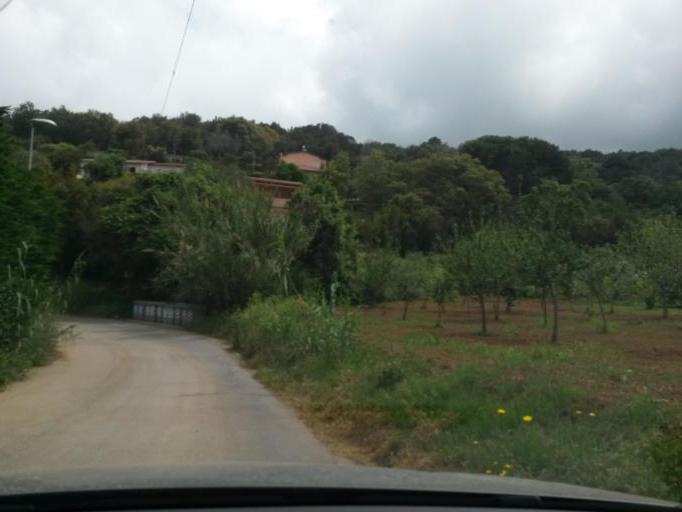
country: IT
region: Tuscany
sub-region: Provincia di Livorno
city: Porto Azzurro
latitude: 42.7464
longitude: 10.4028
